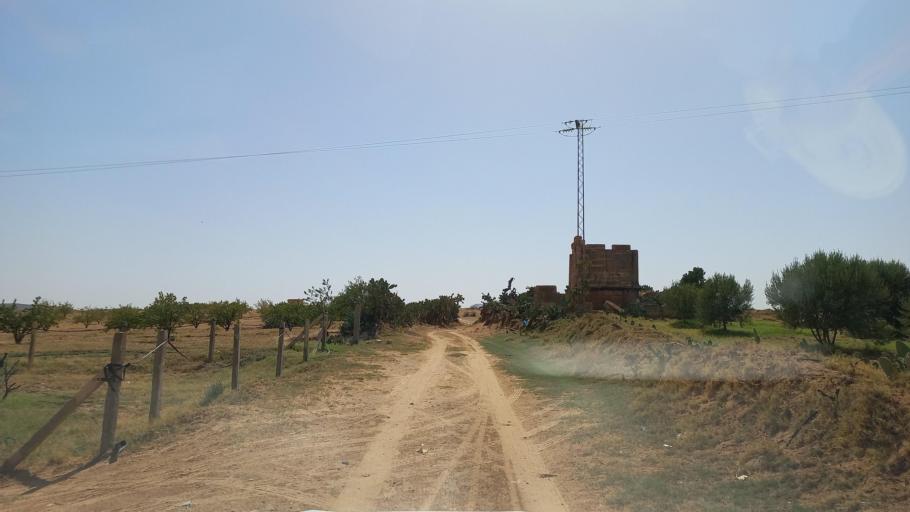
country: TN
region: Al Qasrayn
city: Kasserine
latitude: 35.2260
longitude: 9.0362
